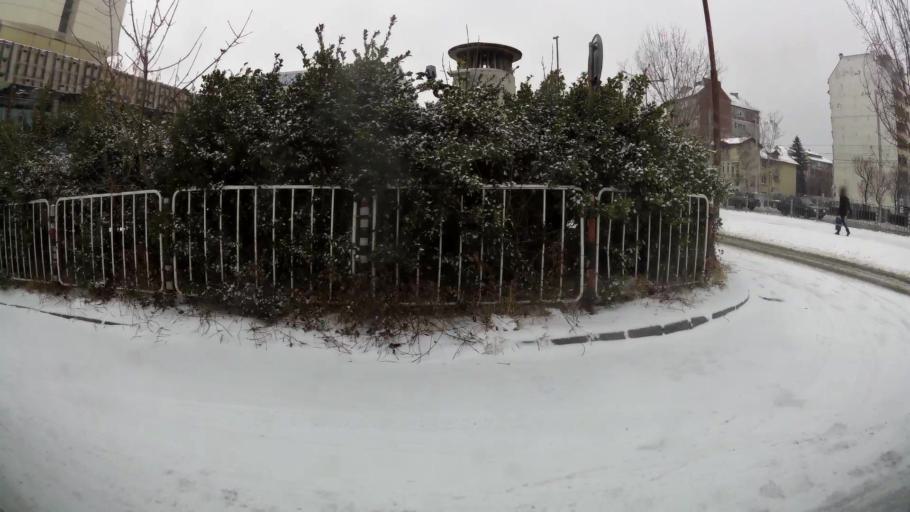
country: BG
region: Sofia-Capital
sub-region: Stolichna Obshtina
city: Sofia
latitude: 42.6916
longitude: 23.3085
